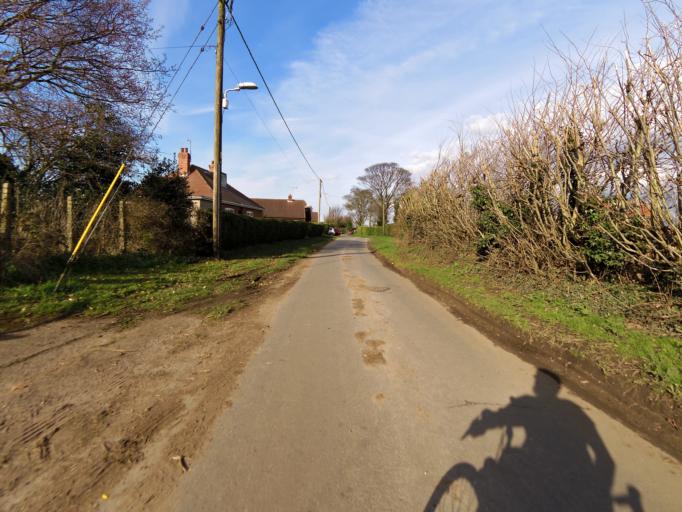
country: GB
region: England
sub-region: East Riding of Yorkshire
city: Pollington
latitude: 53.6691
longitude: -1.0576
